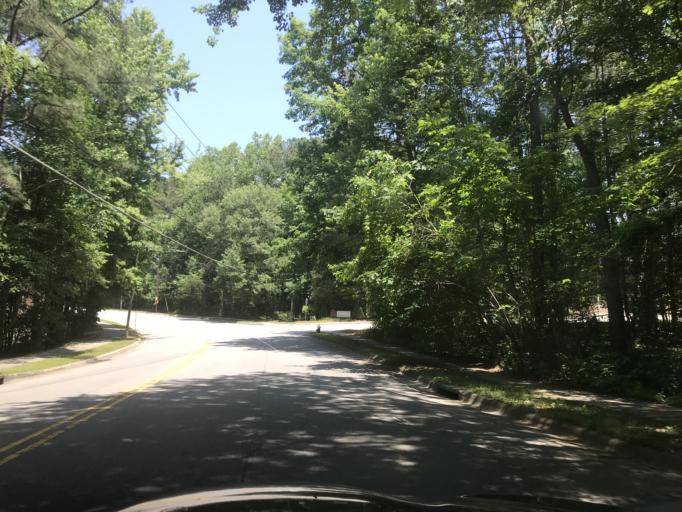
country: US
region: North Carolina
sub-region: Wake County
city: West Raleigh
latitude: 35.8590
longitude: -78.6486
